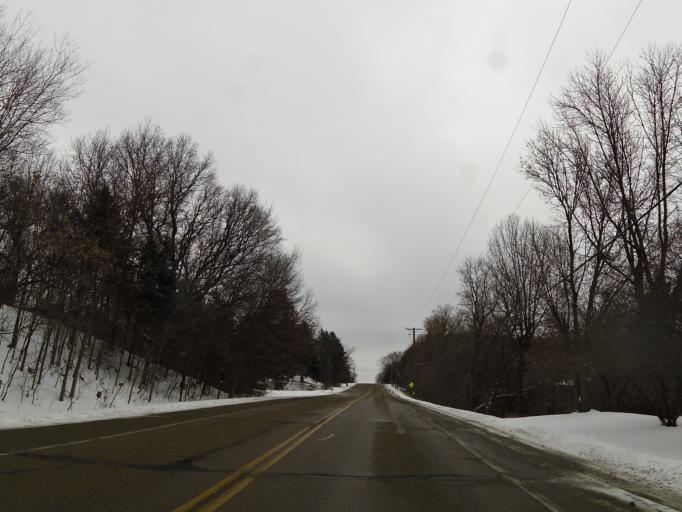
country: US
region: Minnesota
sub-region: Washington County
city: Oak Park Heights
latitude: 45.0051
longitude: -92.8226
